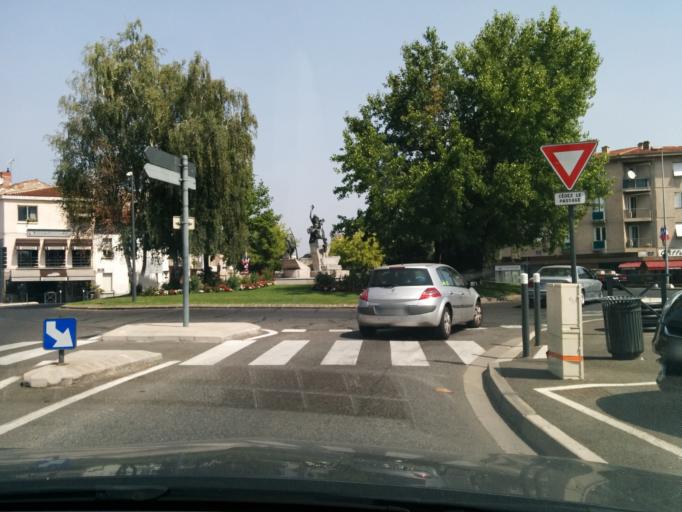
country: FR
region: Midi-Pyrenees
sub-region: Departement du Tarn
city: Albi
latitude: 43.9218
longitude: 2.1494
